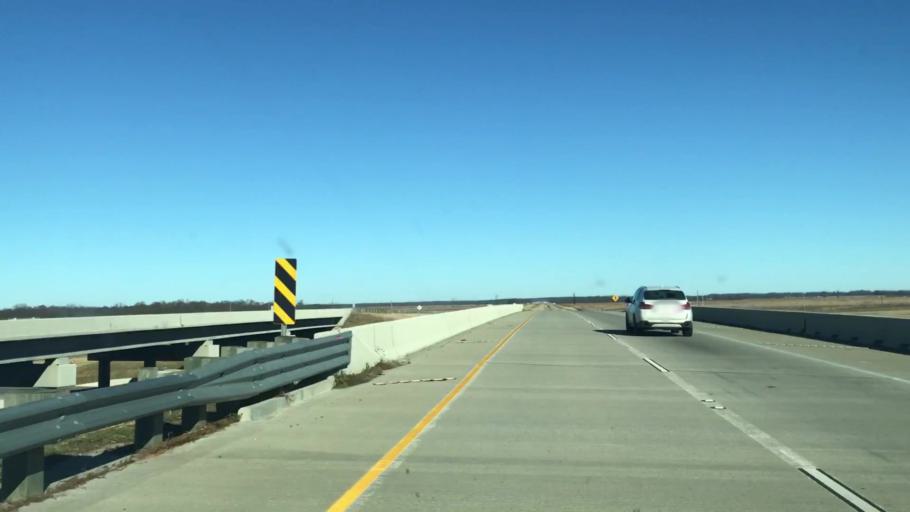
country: US
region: Louisiana
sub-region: Caddo Parish
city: Oil City
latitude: 32.7023
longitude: -93.8613
